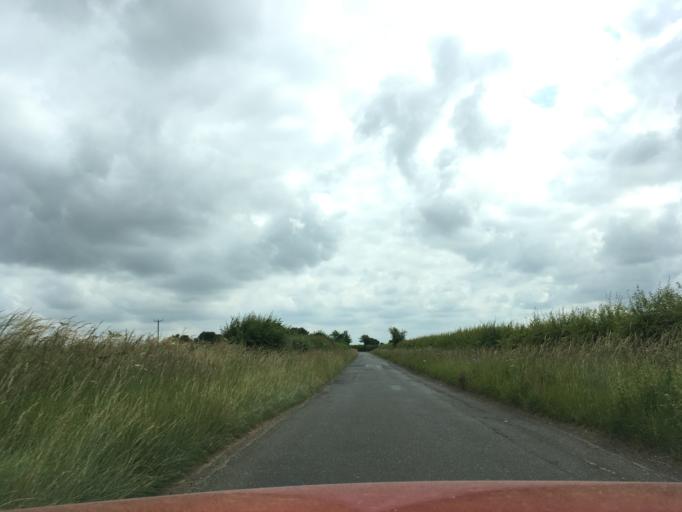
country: GB
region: England
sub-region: Oxfordshire
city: Chipping Norton
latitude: 51.9213
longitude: -1.5304
